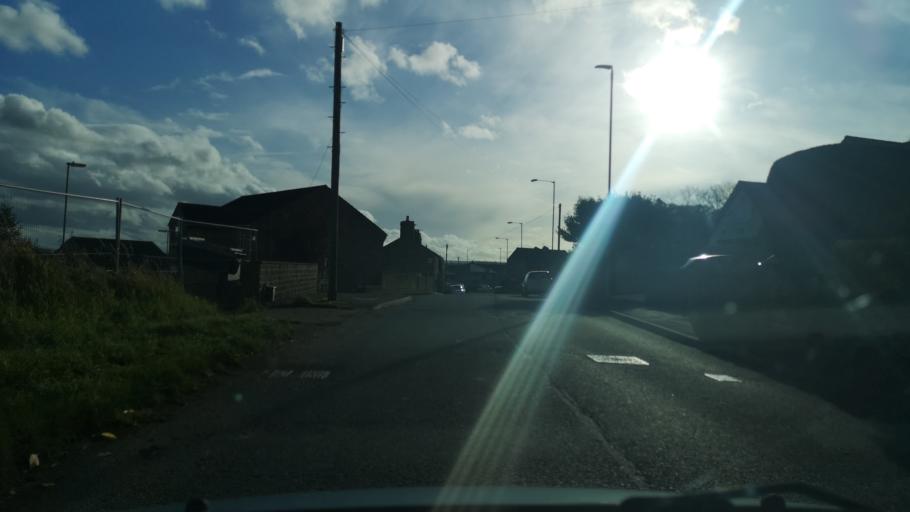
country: GB
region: England
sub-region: City and Borough of Wakefield
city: Middlestown
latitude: 53.6345
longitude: -1.6241
